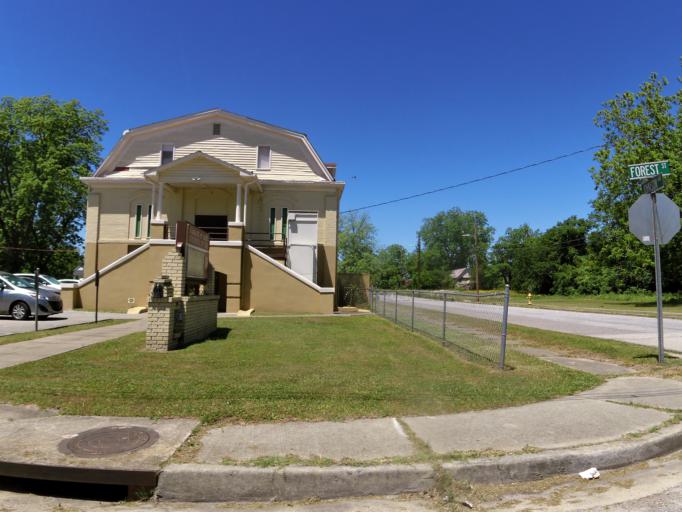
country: US
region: Georgia
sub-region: Richmond County
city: Augusta
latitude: 33.4580
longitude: -81.9833
